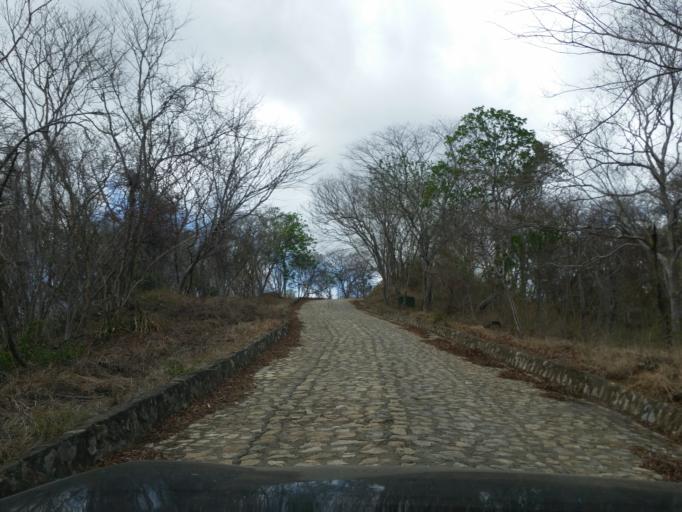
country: NI
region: Rivas
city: Tola
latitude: 11.4298
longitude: -86.0761
